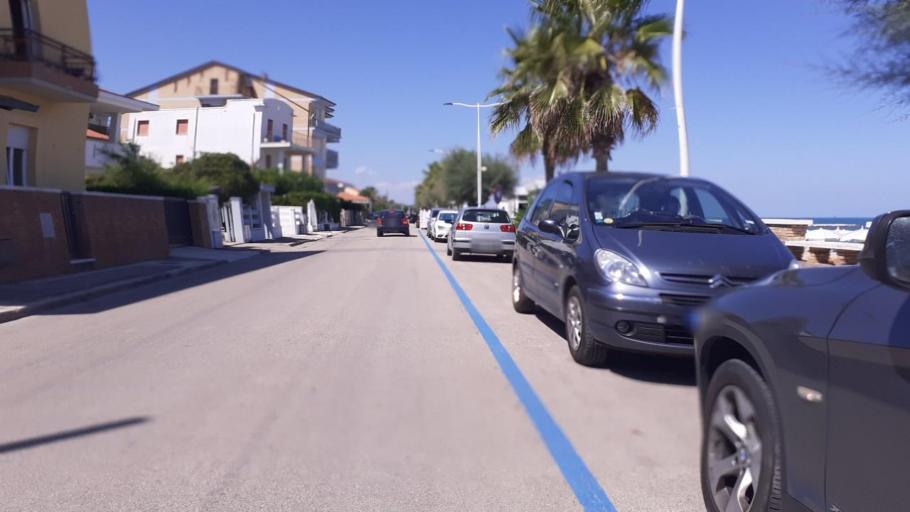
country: IT
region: Abruzzo
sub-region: Provincia di Chieti
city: Casalbordino-Miracoli
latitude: 42.1951
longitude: 14.6324
